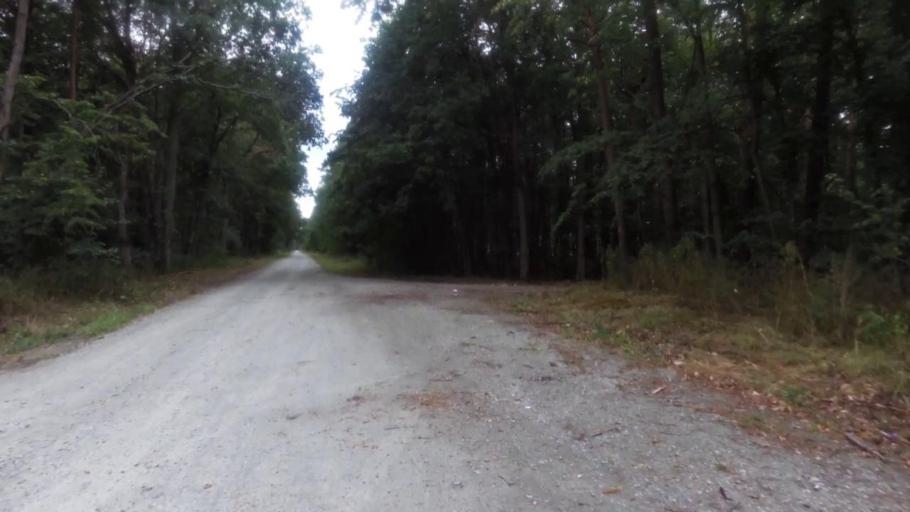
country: PL
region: Lubusz
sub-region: Powiat gorzowski
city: Kostrzyn nad Odra
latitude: 52.6167
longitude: 14.6573
